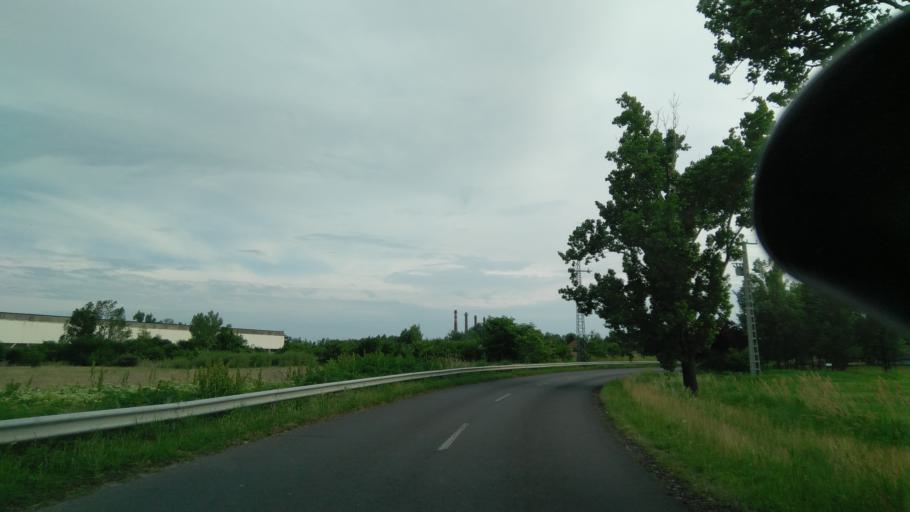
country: HU
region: Bekes
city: Oroshaza
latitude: 46.5867
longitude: 20.6856
